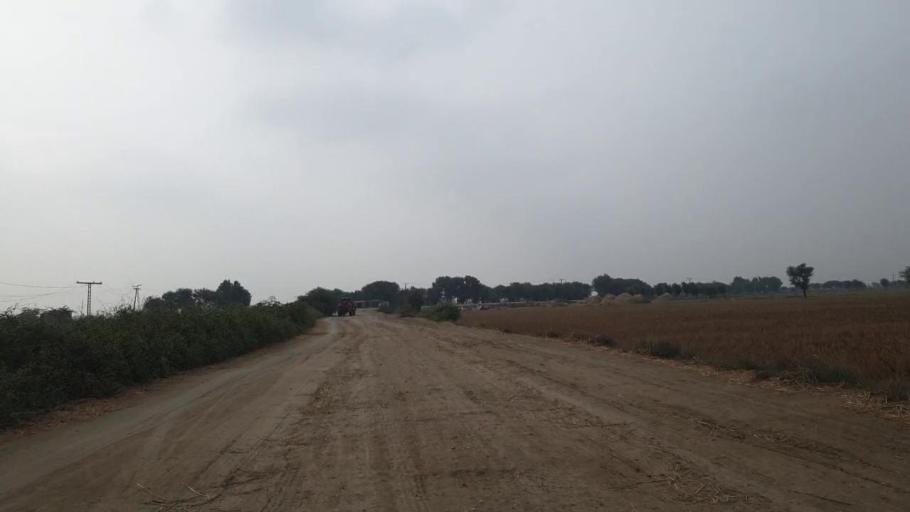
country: PK
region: Sindh
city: Kario
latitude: 24.9365
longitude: 68.5756
